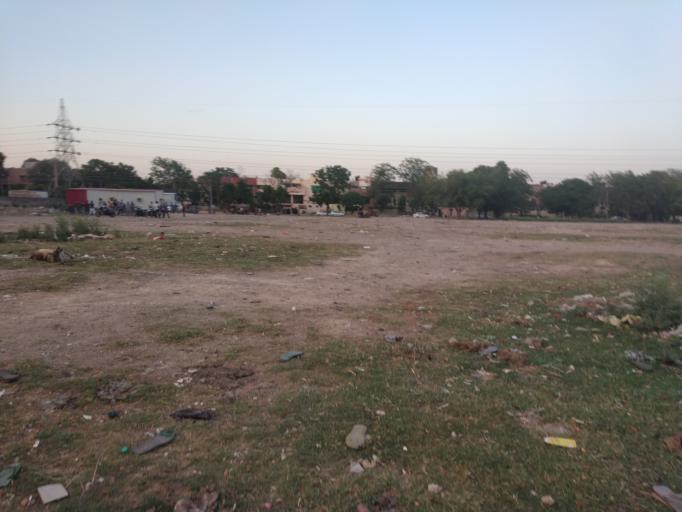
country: IN
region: Punjab
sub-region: Ajitgarh
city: Mohali
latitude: 30.6897
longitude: 76.7287
